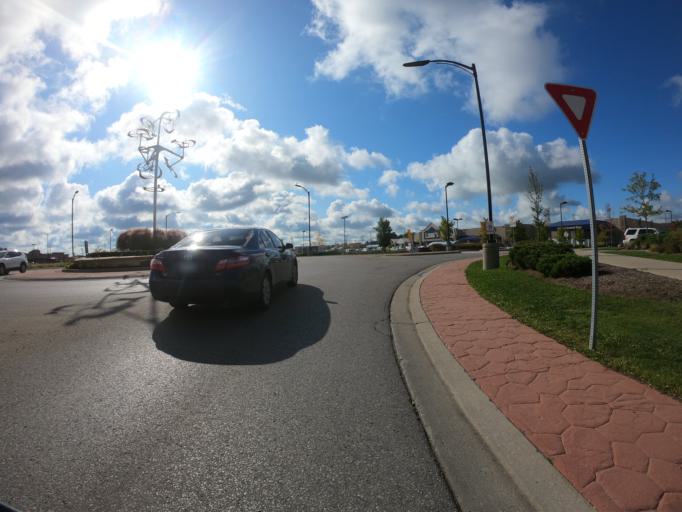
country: CA
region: Ontario
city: Kitchener
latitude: 43.4388
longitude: -80.5642
